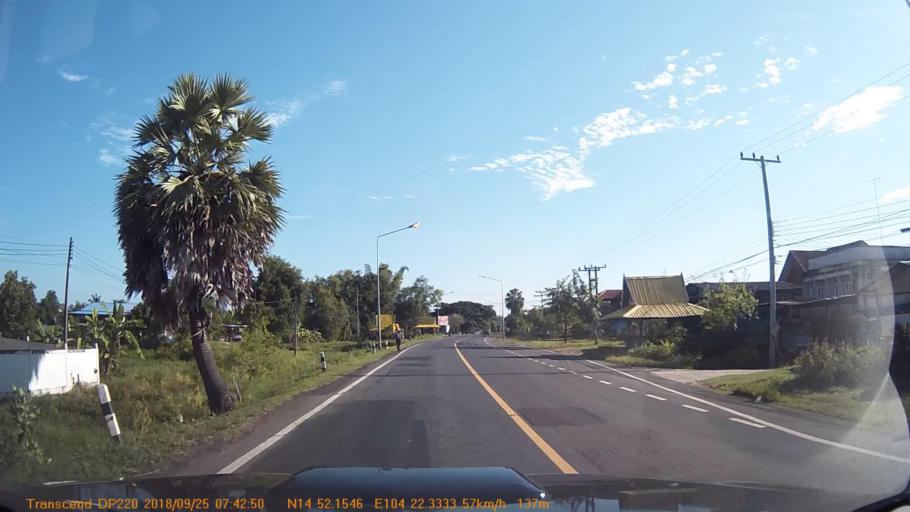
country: TH
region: Sisaket
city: Phayu
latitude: 14.8693
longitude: 104.3722
